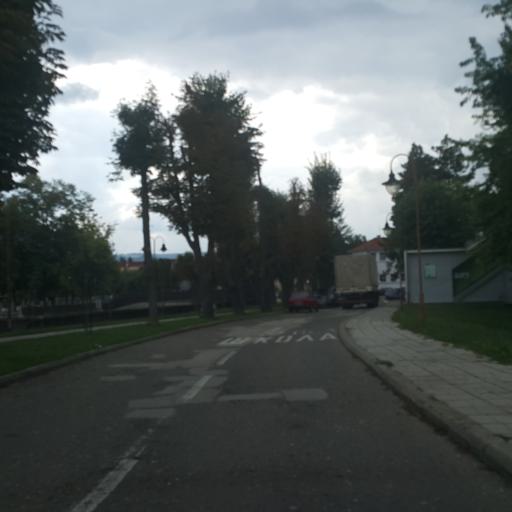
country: RS
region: Central Serbia
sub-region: Zajecarski Okrug
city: Knjazevac
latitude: 43.5697
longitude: 22.2556
